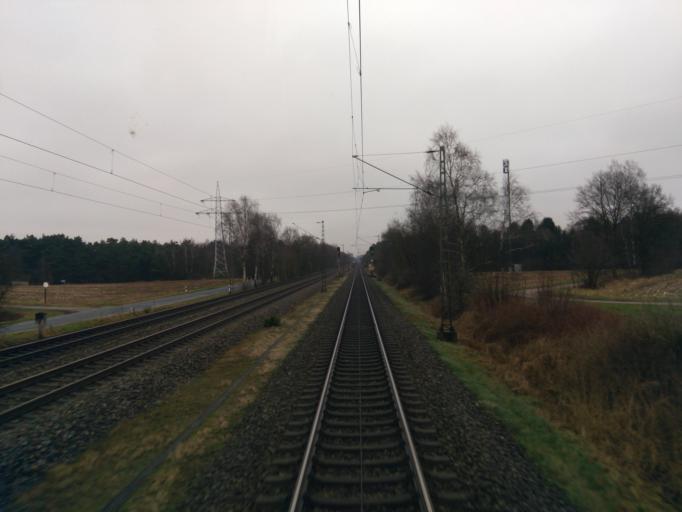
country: DE
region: Lower Saxony
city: Kakenstorf
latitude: 53.2829
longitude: 9.7557
